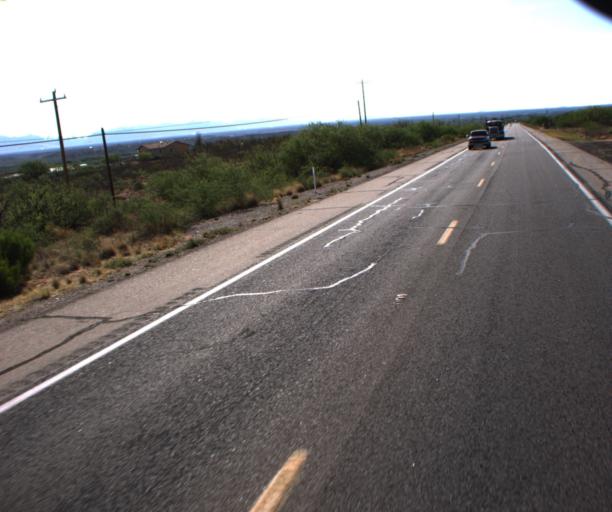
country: US
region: Arizona
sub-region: Cochise County
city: Benson
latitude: 31.9264
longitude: -110.2760
